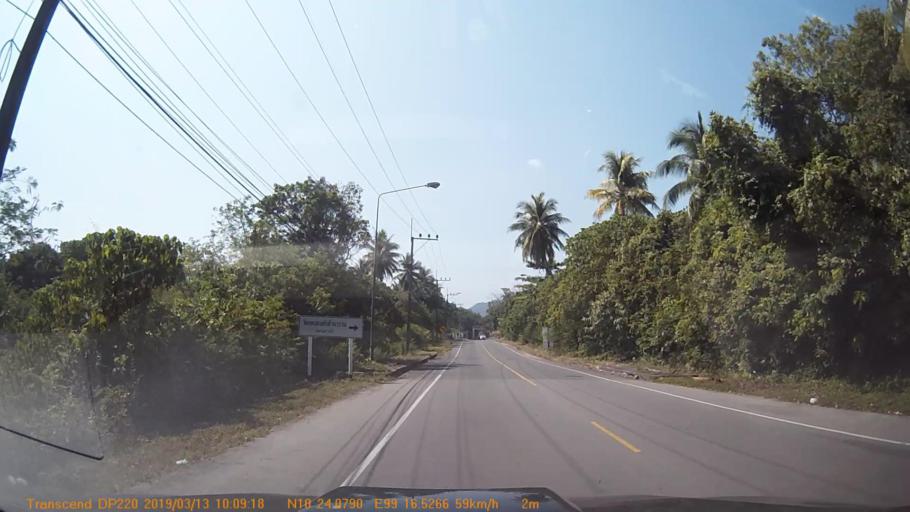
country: TH
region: Chumphon
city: Chumphon
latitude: 10.4013
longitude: 99.2754
